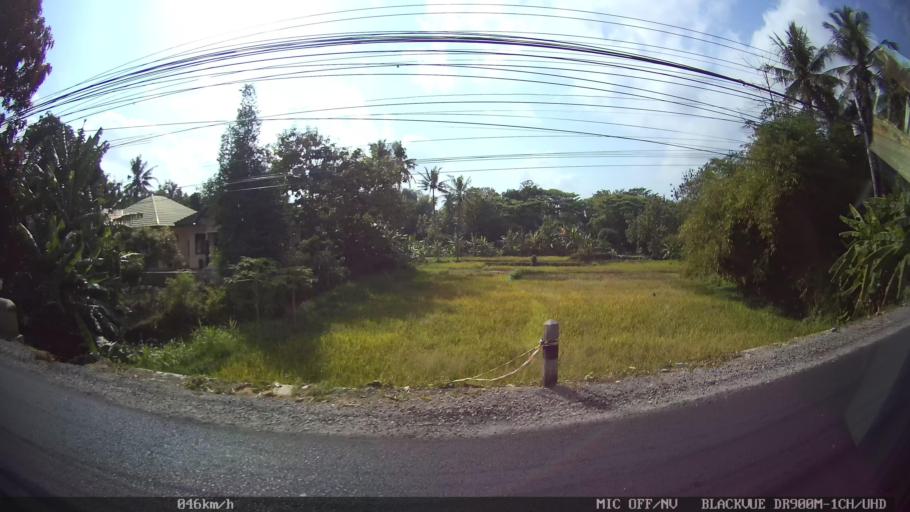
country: ID
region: Daerah Istimewa Yogyakarta
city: Godean
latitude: -7.8327
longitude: 110.2209
